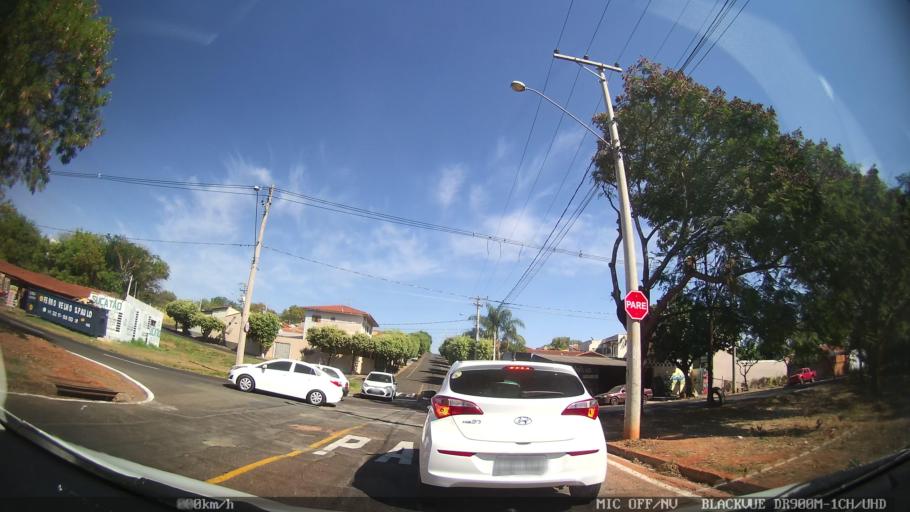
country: BR
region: Sao Paulo
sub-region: Sao Jose Do Rio Preto
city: Sao Jose do Rio Preto
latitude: -20.7737
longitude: -49.4009
